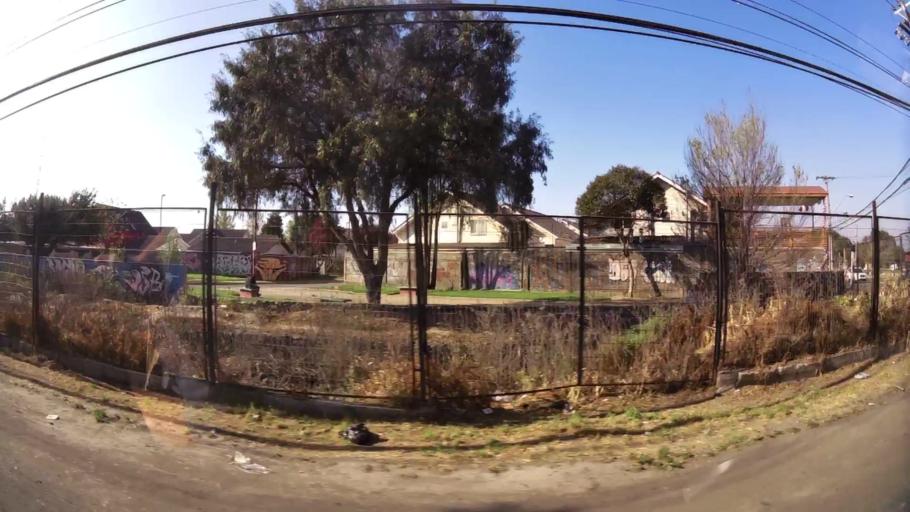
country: CL
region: Santiago Metropolitan
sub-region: Provincia de Santiago
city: Lo Prado
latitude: -33.4892
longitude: -70.7750
